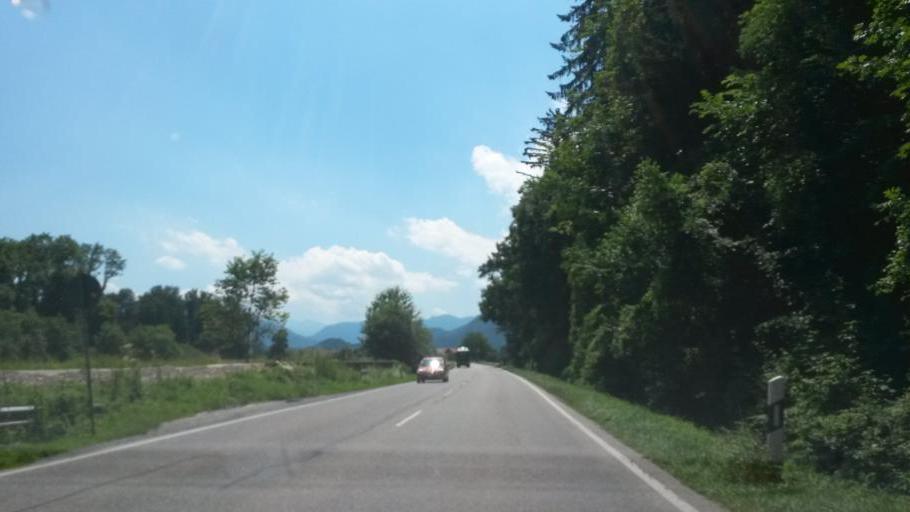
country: DE
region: Bavaria
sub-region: Upper Bavaria
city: Staudach-Egerndach
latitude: 47.7883
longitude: 12.4782
